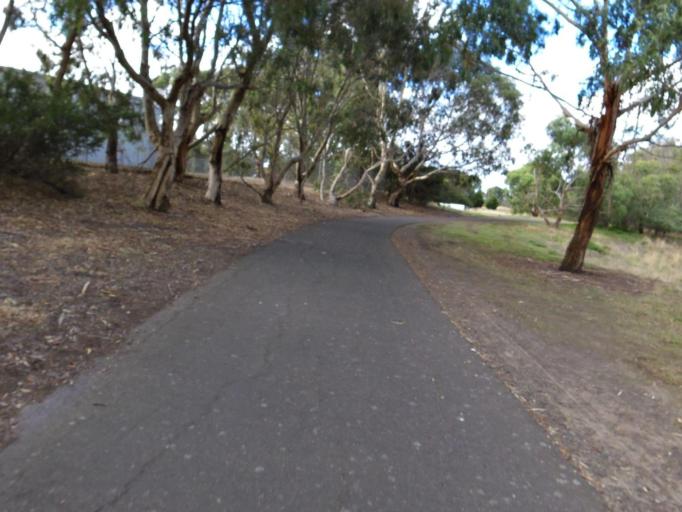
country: AU
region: Victoria
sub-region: Greater Geelong
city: Wandana Heights
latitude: -38.2054
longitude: 144.3081
